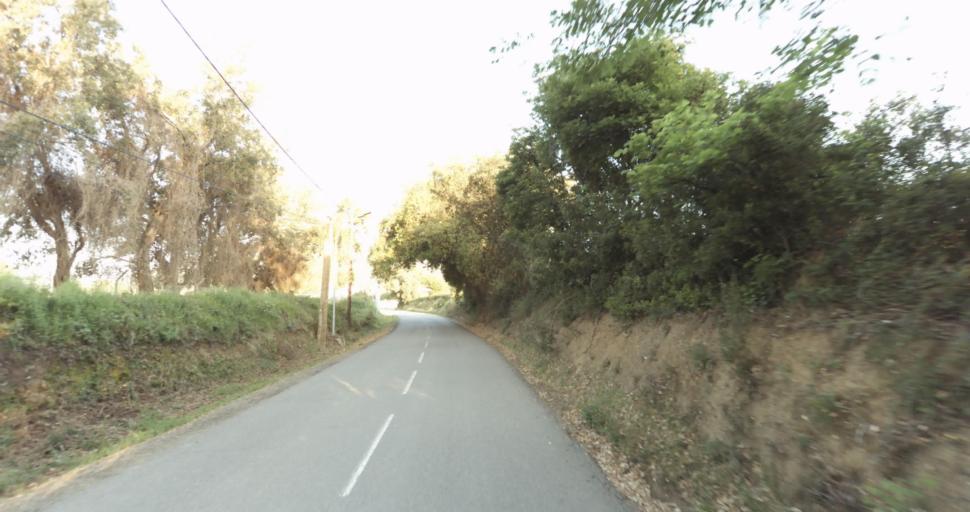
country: FR
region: Corsica
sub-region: Departement de la Haute-Corse
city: Biguglia
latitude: 42.6197
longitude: 9.4409
